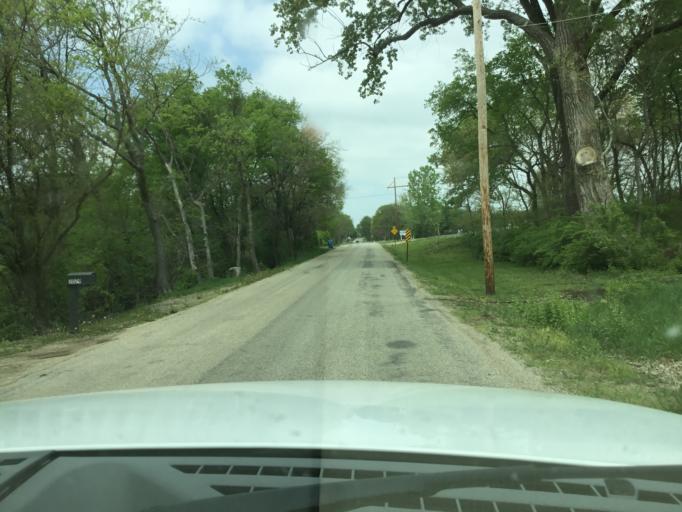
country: US
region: Kansas
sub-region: Shawnee County
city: Topeka
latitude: 39.0124
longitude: -95.5861
